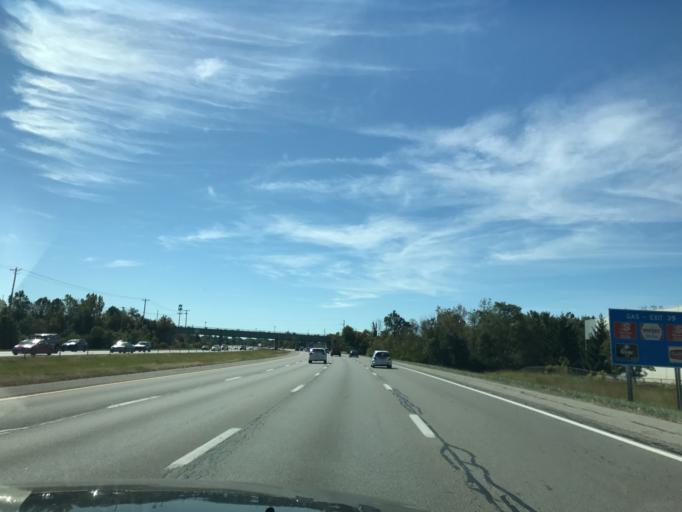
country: US
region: Ohio
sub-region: Franklin County
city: Gahanna
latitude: 39.9902
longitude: -82.8572
